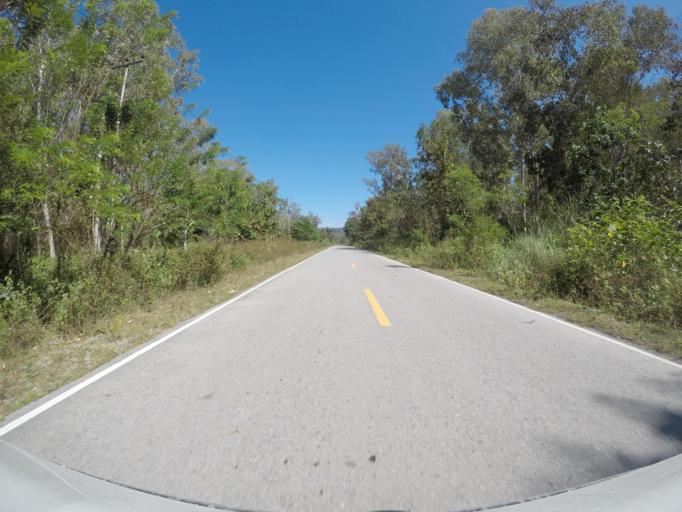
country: TL
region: Viqueque
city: Viqueque
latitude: -8.9629
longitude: 126.0167
